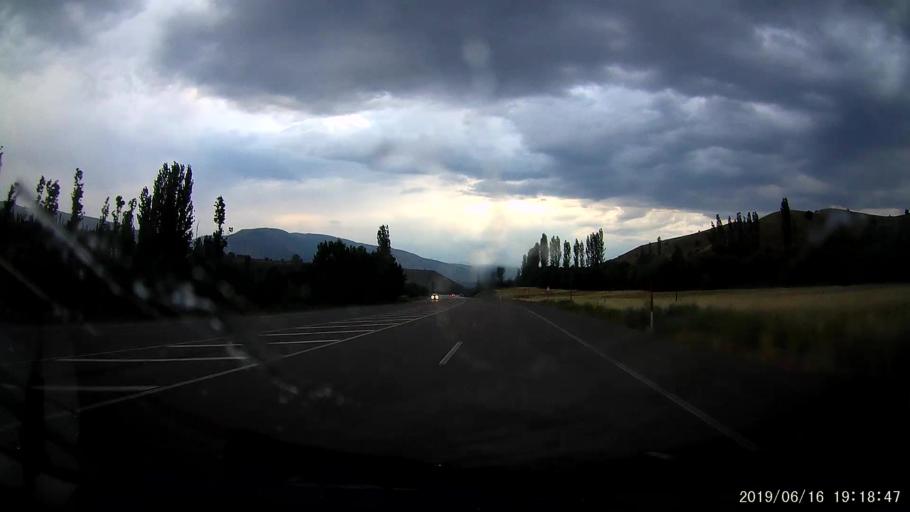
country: TR
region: Sivas
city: Akincilar
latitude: 40.0949
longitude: 38.4479
